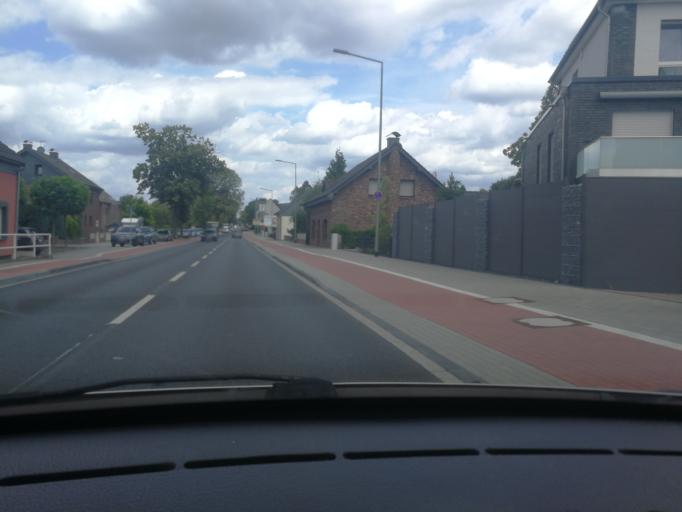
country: DE
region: North Rhine-Westphalia
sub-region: Regierungsbezirk Dusseldorf
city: Moers
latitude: 51.3952
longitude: 6.6573
